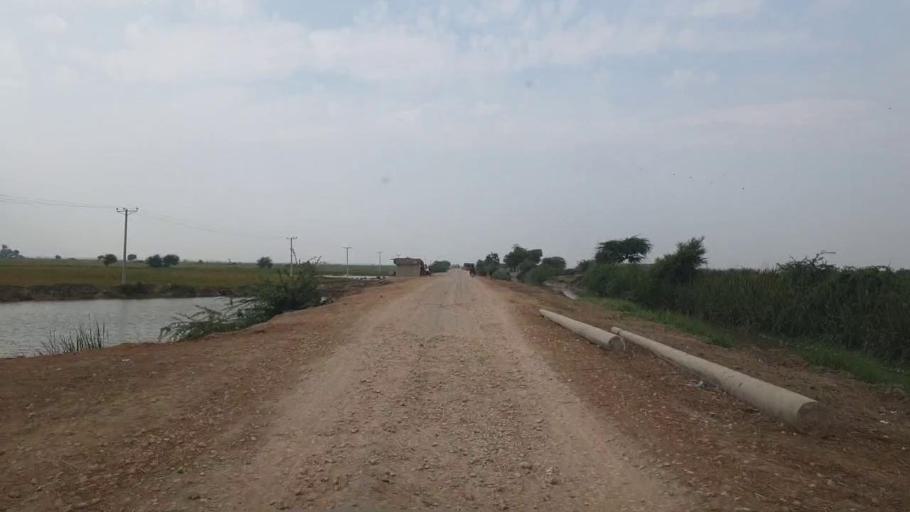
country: PK
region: Sindh
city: Kario
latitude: 24.6085
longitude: 68.5946
